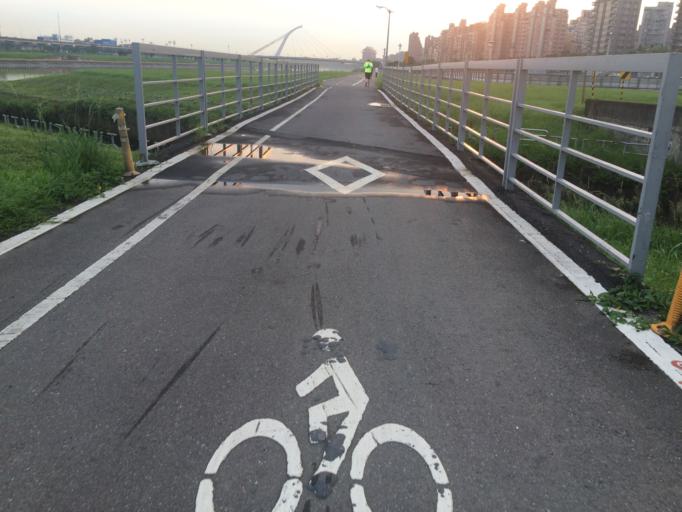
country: TW
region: Taipei
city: Taipei
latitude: 25.0763
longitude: 121.5558
